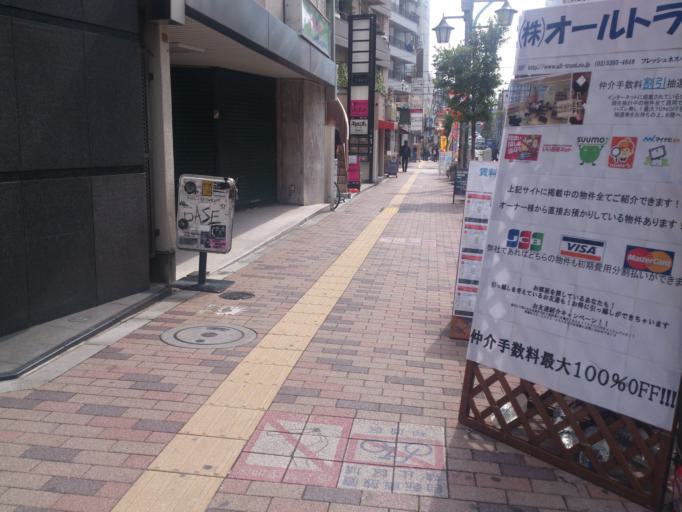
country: JP
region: Tokyo
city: Tokyo
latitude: 35.7038
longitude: 139.6497
